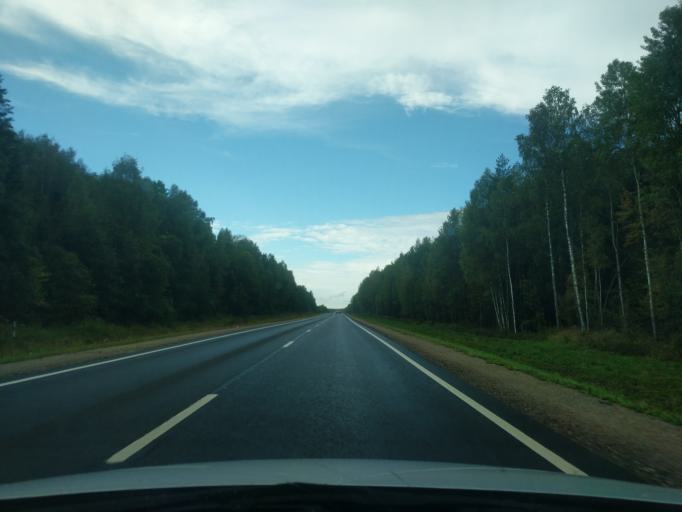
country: RU
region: Kostroma
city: Ostrovskoye
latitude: 57.8141
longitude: 42.0152
